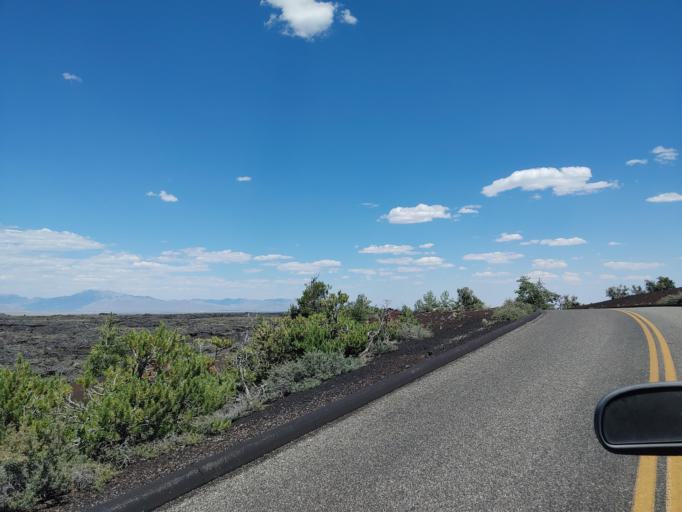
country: US
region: Idaho
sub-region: Butte County
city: Arco
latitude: 43.4533
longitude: -113.5551
